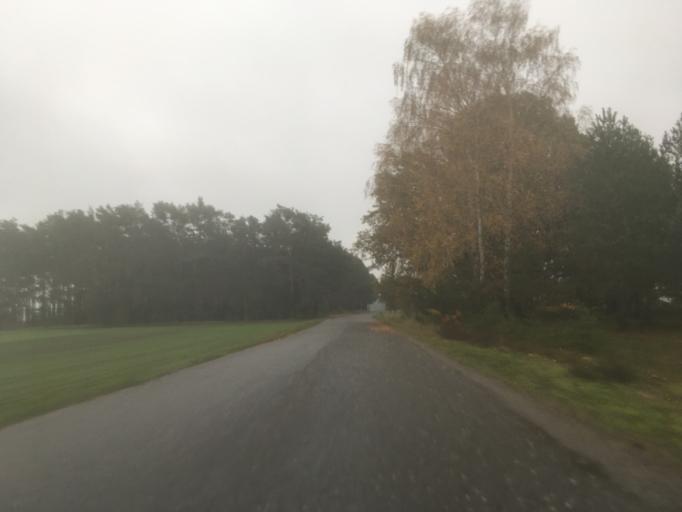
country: DE
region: Brandenburg
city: Schlepzig
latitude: 52.0170
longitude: 13.9404
